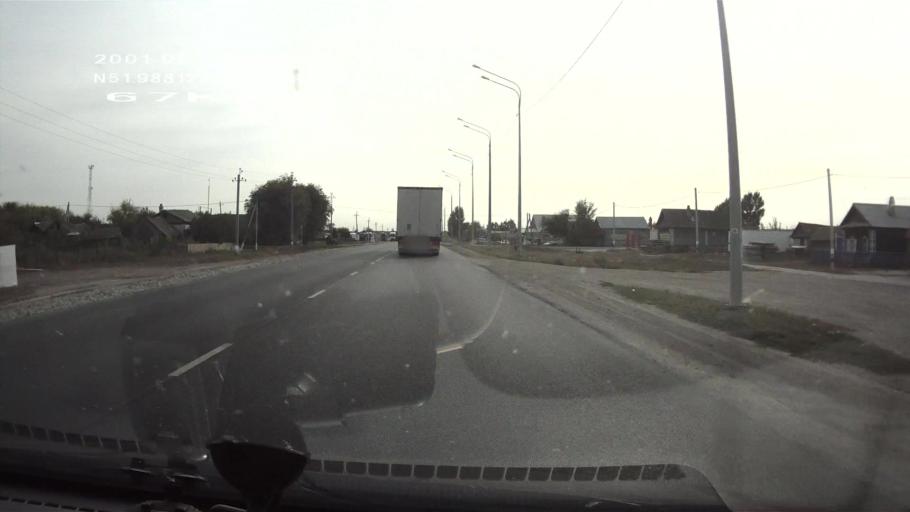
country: RU
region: Saratov
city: Sinodskoye
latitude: 51.9877
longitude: 46.6653
